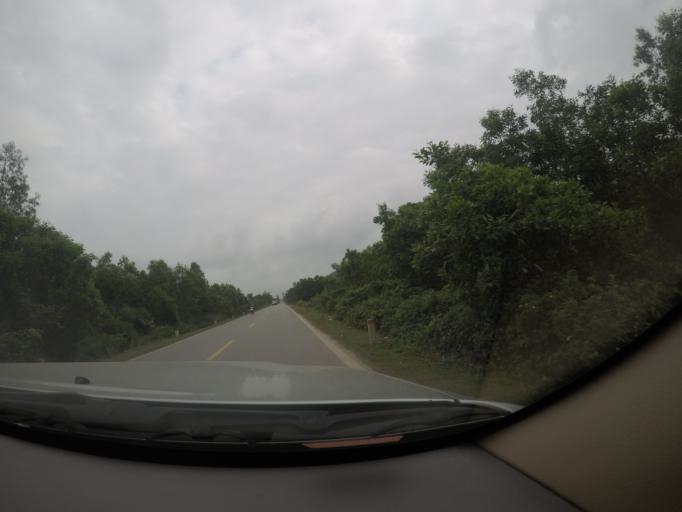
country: VN
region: Quang Binh
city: Quan Hau
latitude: 17.2778
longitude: 106.6538
